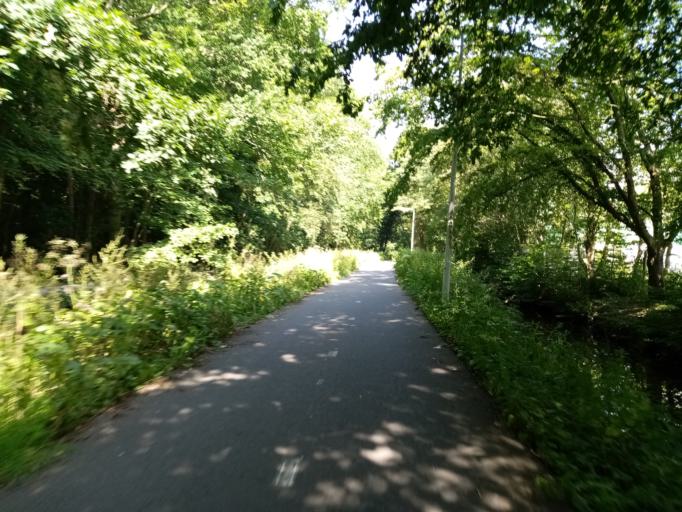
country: NL
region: South Holland
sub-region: Gemeente Oegstgeest
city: Oegstgeest
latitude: 52.1757
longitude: 4.4828
